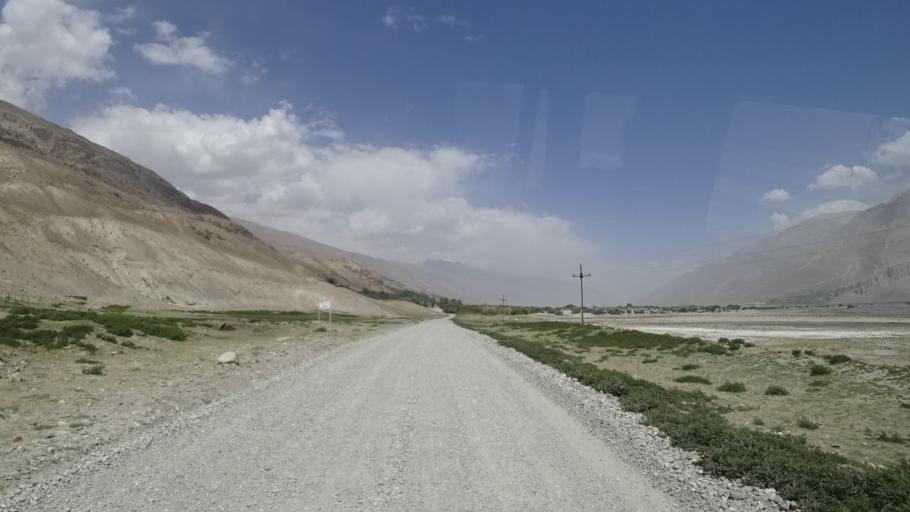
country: AF
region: Badakhshan
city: Khandud
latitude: 36.9310
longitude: 72.2083
